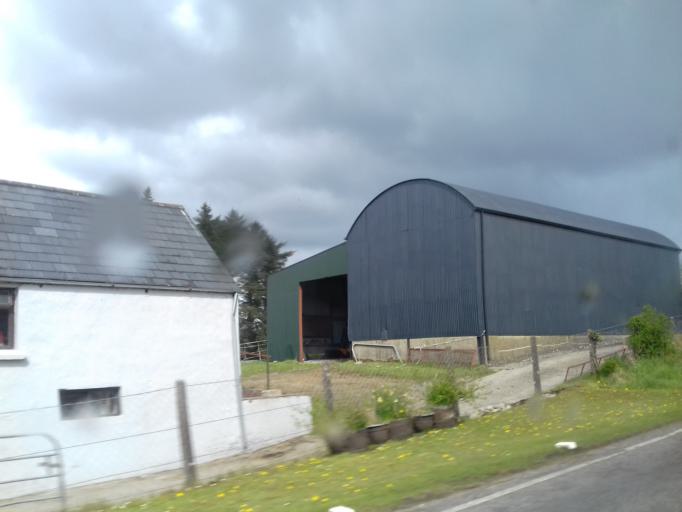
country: IE
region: Ulster
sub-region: County Donegal
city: Ballyshannon
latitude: 54.4699
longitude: -7.9877
